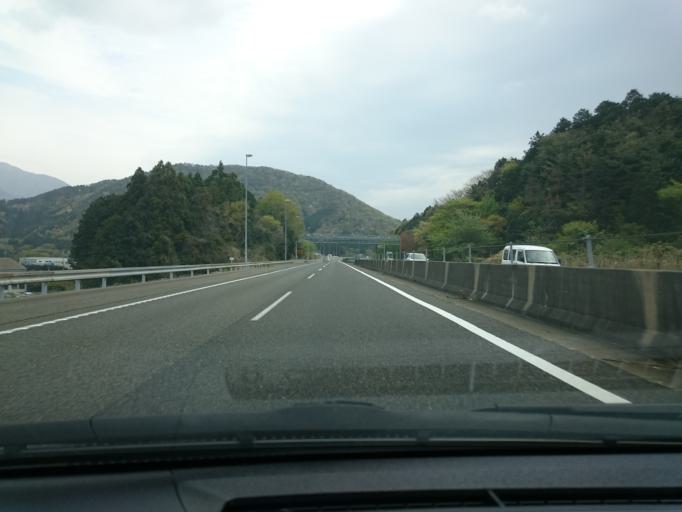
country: JP
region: Gifu
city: Tarui
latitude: 35.3411
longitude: 136.4069
